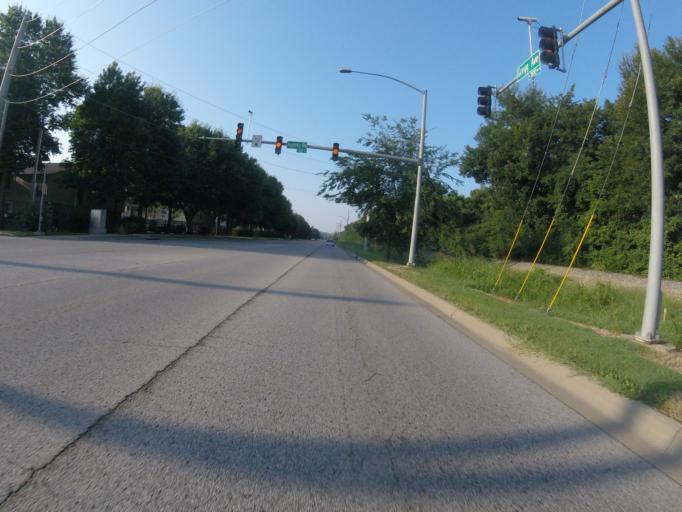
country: US
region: Arkansas
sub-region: Washington County
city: Johnson
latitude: 36.1082
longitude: -94.1636
